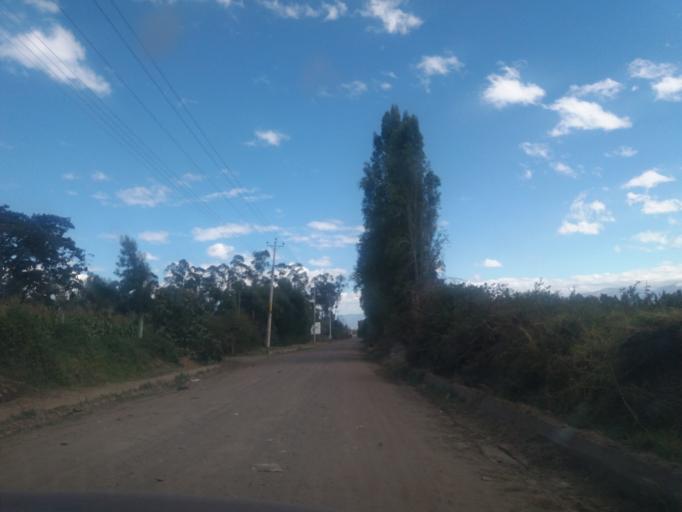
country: EC
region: Pichincha
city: Sangolqui
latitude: -0.1780
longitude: -78.3375
